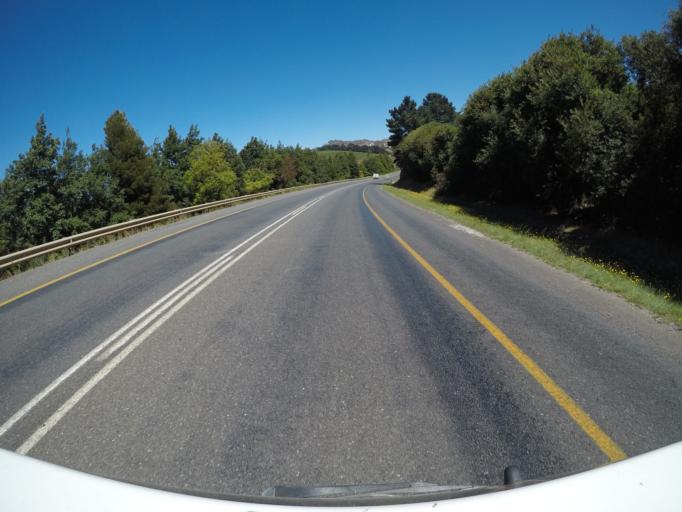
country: ZA
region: Western Cape
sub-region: Overberg District Municipality
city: Grabouw
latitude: -34.1649
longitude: 19.0235
